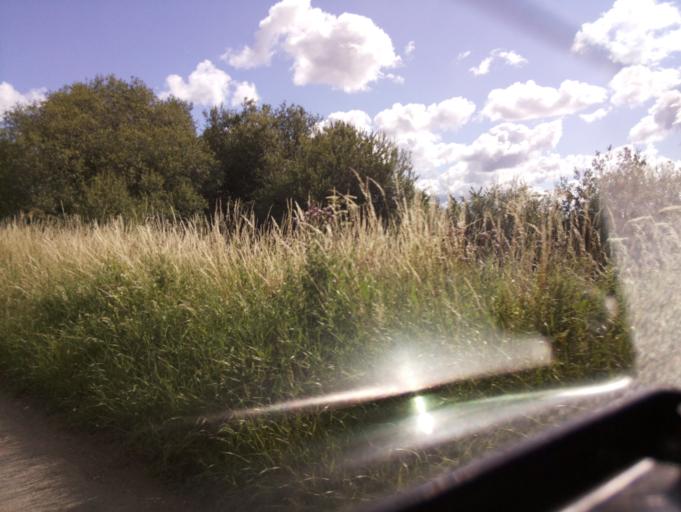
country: GB
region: England
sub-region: Gloucestershire
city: Newent
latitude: 51.8596
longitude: -2.3527
